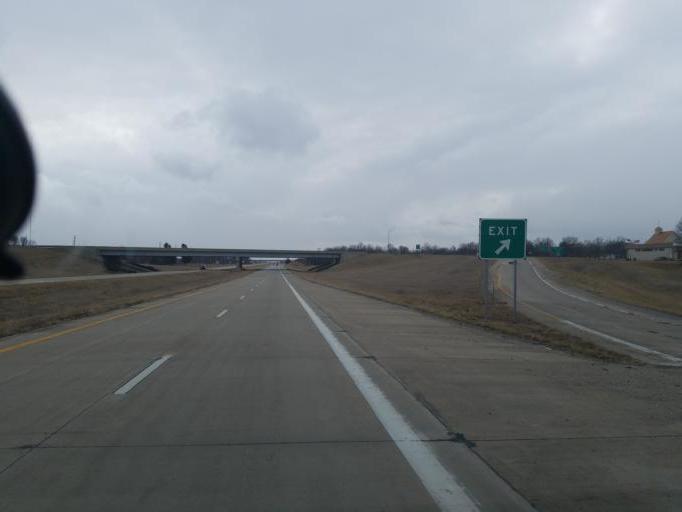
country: US
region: Missouri
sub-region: Randolph County
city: Moberly
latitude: 39.4190
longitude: -92.4121
